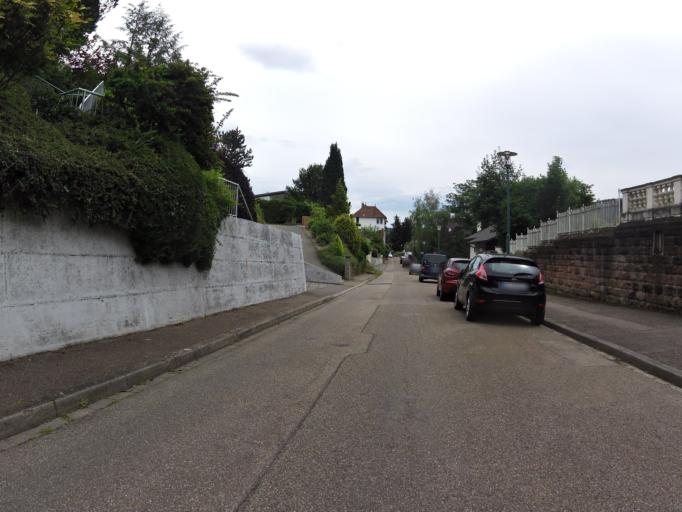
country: DE
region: Baden-Wuerttemberg
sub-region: Freiburg Region
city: Lahr
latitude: 48.3418
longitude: 7.8880
